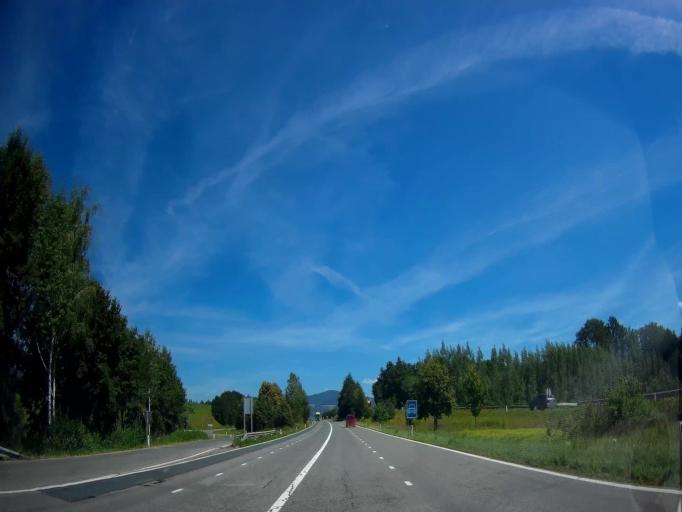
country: AT
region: Carinthia
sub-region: Politischer Bezirk Sankt Veit an der Glan
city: Molbling
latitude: 46.8403
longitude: 14.4469
